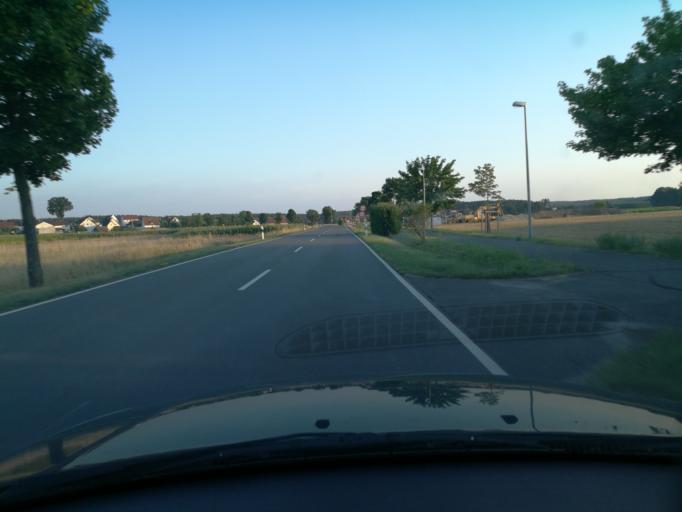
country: DE
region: Bavaria
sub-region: Regierungsbezirk Mittelfranken
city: Hessdorf
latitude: 49.6212
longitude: 10.9079
